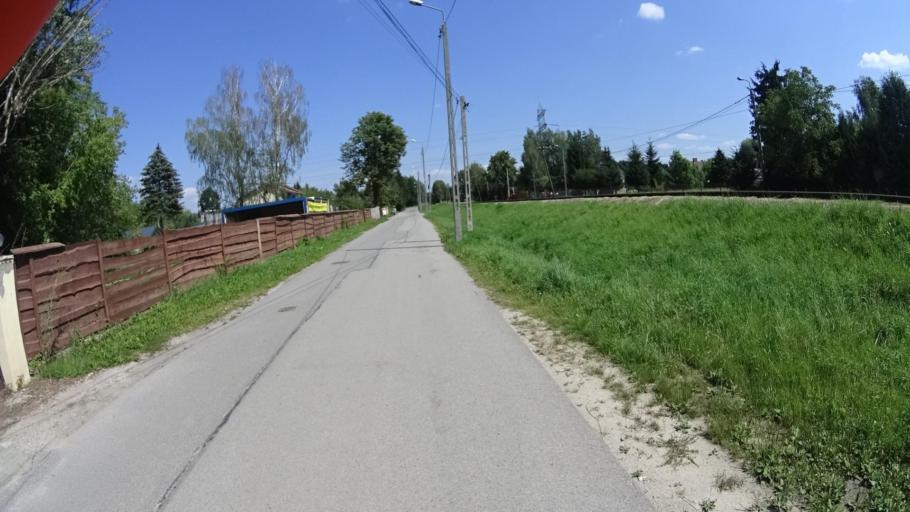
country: PL
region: Masovian Voivodeship
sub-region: Powiat piaseczynski
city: Tarczyn
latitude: 52.0022
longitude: 20.9072
